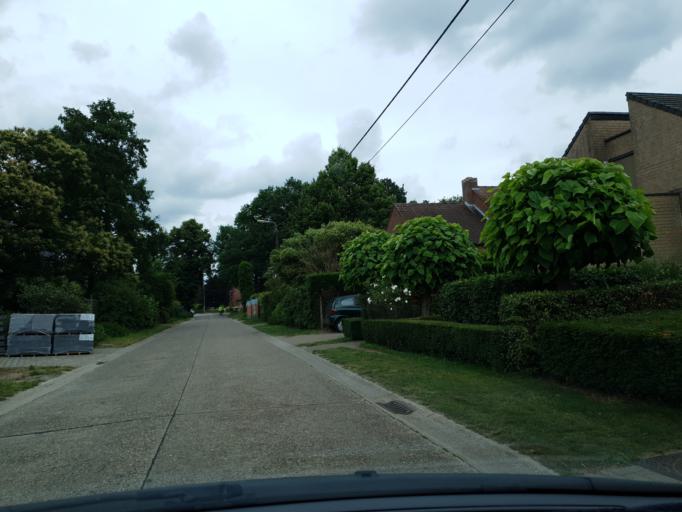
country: BE
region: Flanders
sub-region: Provincie Antwerpen
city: Westerlo
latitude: 51.0989
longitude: 4.9025
